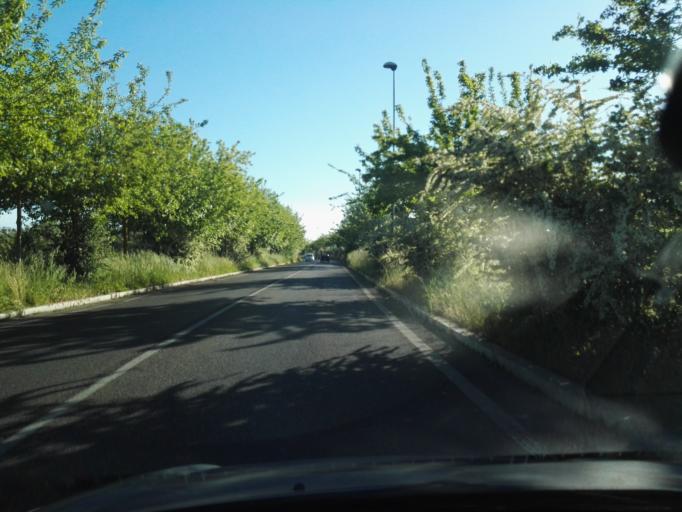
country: IT
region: Latium
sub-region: Citta metropolitana di Roma Capitale
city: Selcetta
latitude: 41.7785
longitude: 12.4721
